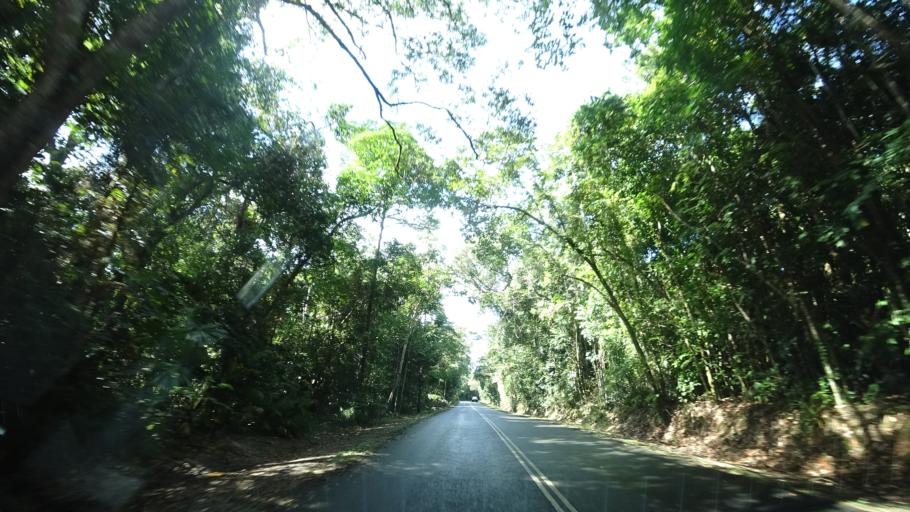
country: AU
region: Queensland
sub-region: Cairns
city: Port Douglas
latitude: -16.1439
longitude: 145.4374
